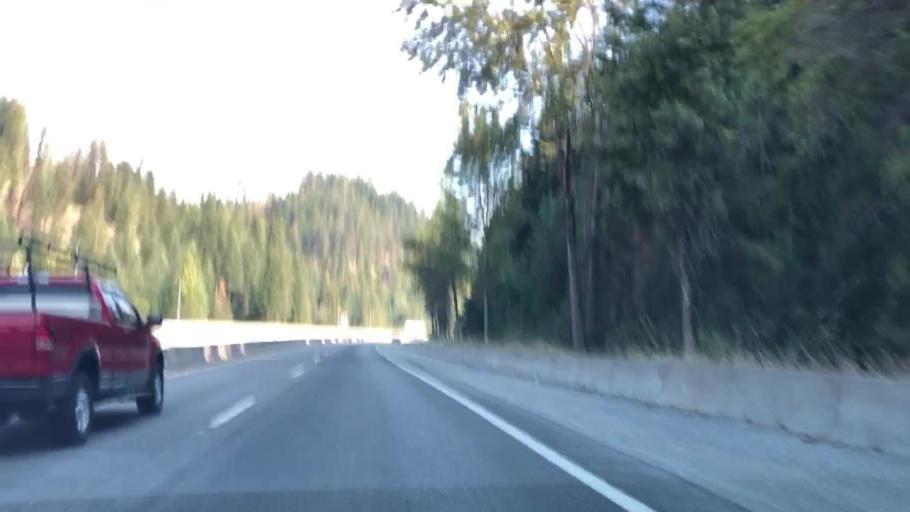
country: US
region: Idaho
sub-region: Shoshone County
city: Pinehurst
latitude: 47.5882
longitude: -116.4794
